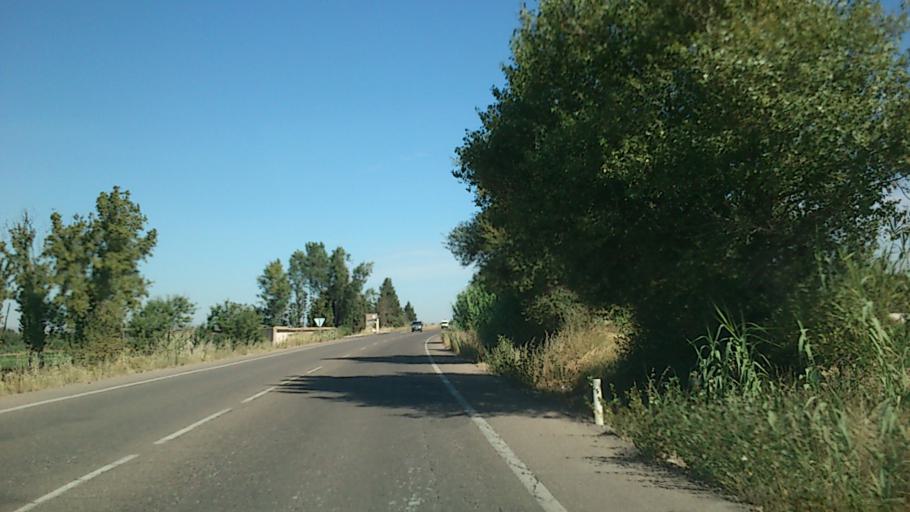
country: ES
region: Aragon
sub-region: Provincia de Zaragoza
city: Villanueva de Gallego
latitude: 41.7314
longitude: -0.8089
